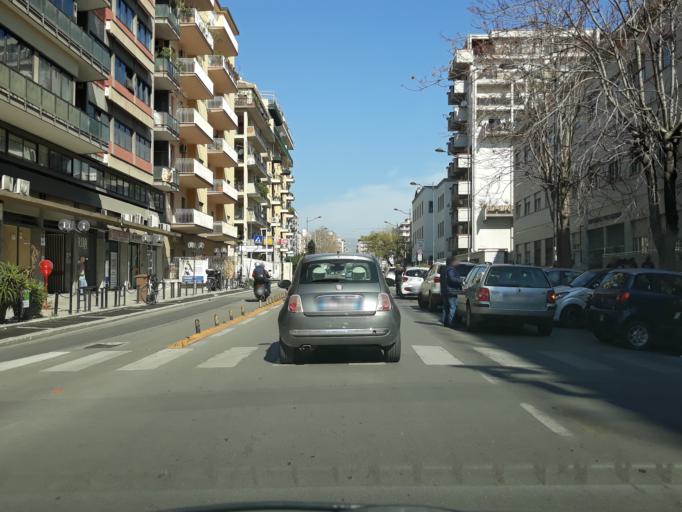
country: IT
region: Sicily
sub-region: Palermo
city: Palermo
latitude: 38.1365
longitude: 13.3508
